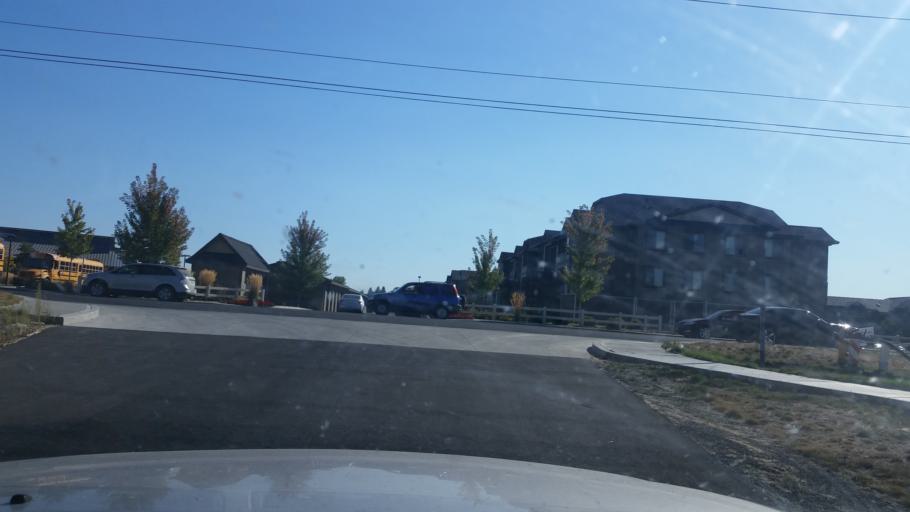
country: US
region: Washington
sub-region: Spokane County
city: Cheney
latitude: 47.5076
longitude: -117.5812
